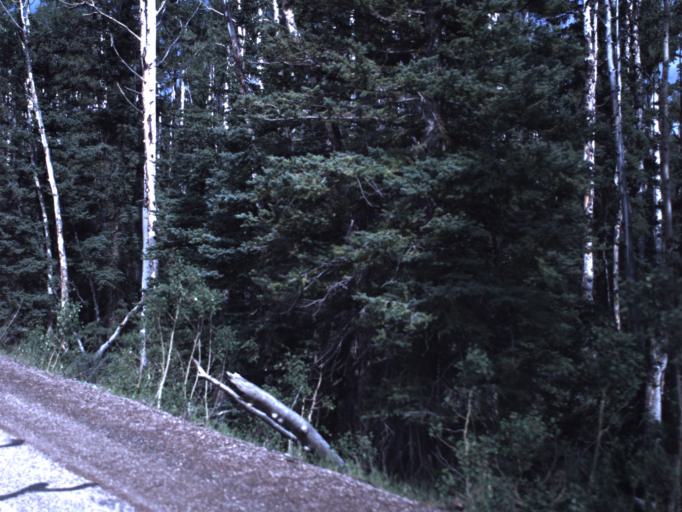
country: US
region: Utah
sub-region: Iron County
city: Parowan
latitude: 37.5198
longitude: -112.7074
